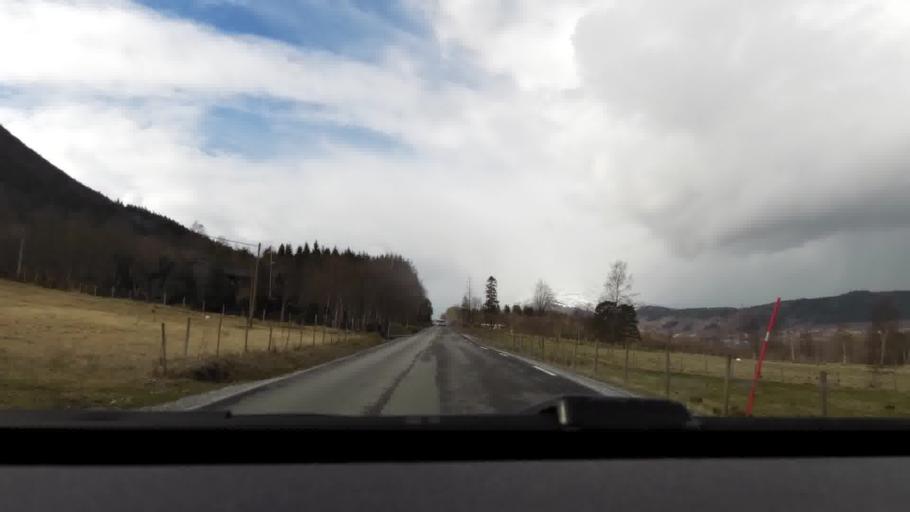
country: NO
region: More og Romsdal
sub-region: Averoy
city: Bruhagen
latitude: 63.1095
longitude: 7.6347
